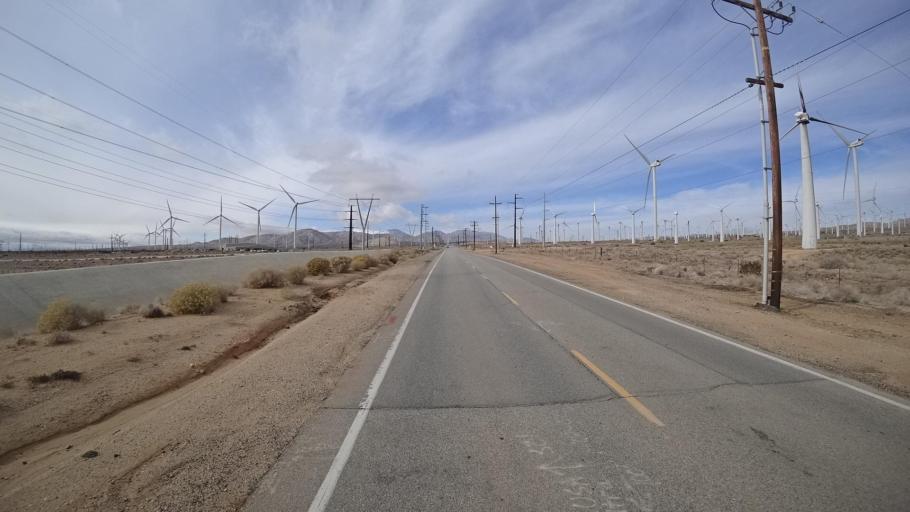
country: US
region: California
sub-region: Kern County
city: Mojave
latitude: 35.0384
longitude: -118.2817
